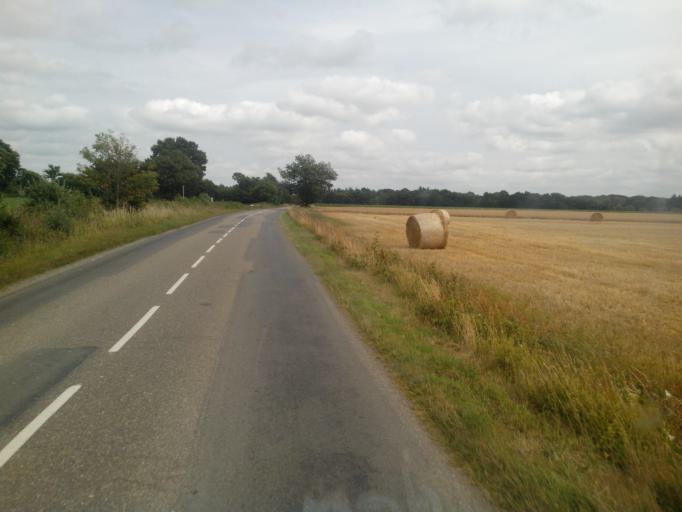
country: FR
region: Brittany
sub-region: Departement d'Ille-et-Vilaine
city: Maxent
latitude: 47.9904
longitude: -2.0643
